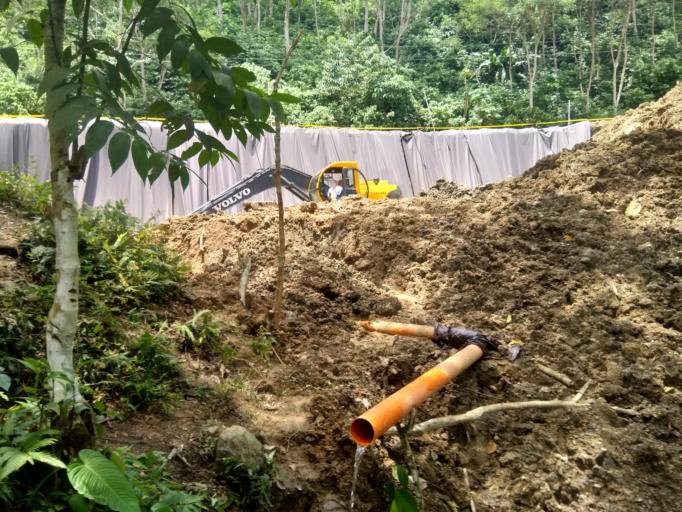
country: PH
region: Davao
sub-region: Province of Davao del Norte
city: Santo Nino
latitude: 7.6327
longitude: 125.5515
